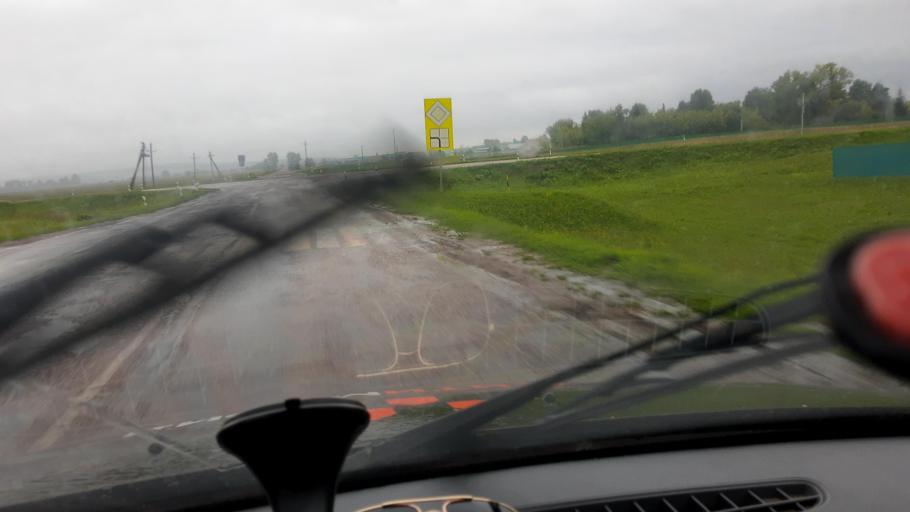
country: RU
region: Bashkortostan
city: Karmaskaly
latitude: 53.9763
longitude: 56.3878
